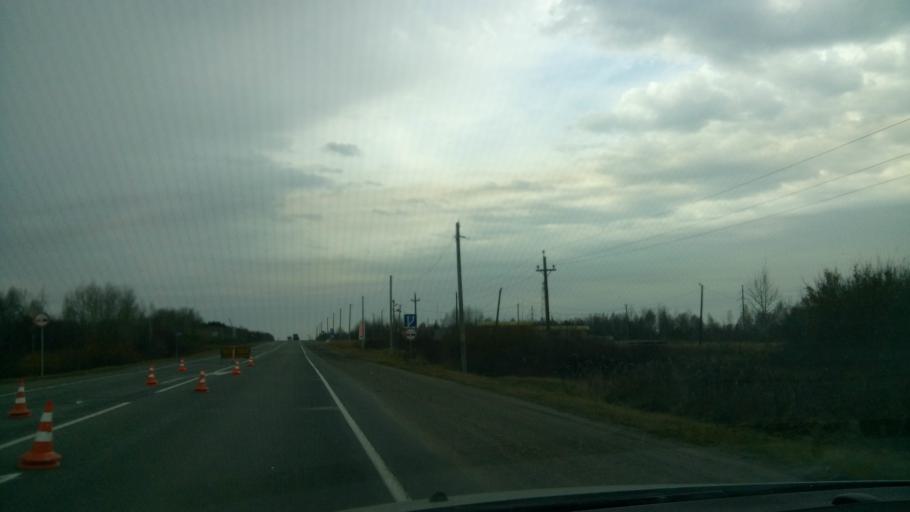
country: RU
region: Sverdlovsk
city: Obukhovskoye
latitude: 56.8522
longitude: 62.6051
